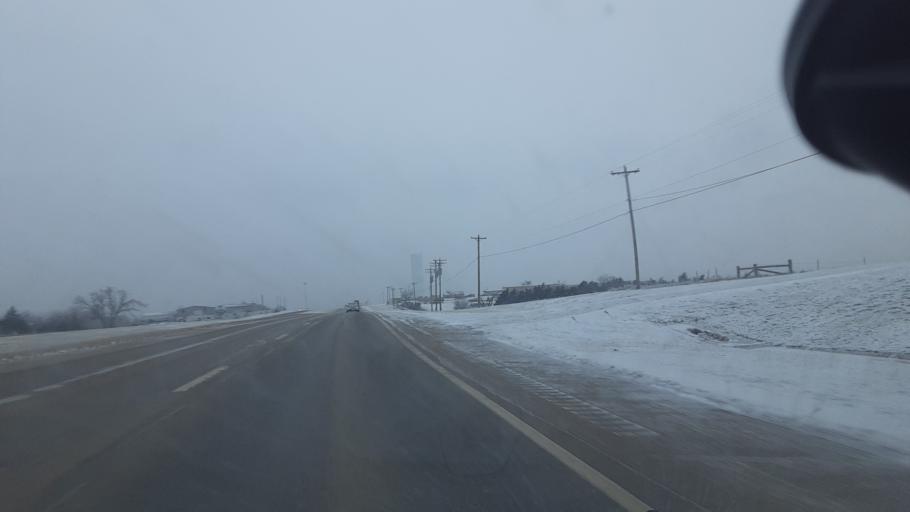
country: US
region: Oklahoma
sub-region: Logan County
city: Guthrie
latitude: 35.8851
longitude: -97.3743
